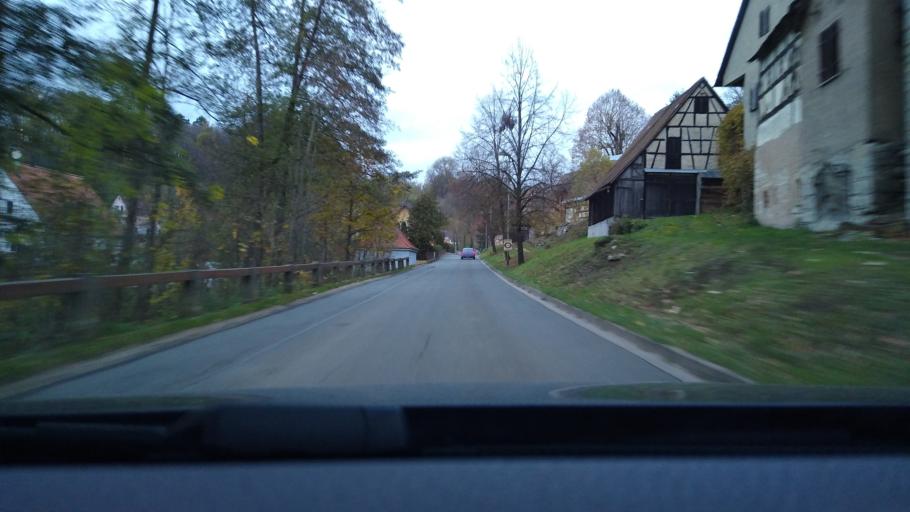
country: DE
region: Bavaria
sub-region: Upper Franconia
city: Grafenberg
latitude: 49.6475
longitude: 11.2494
